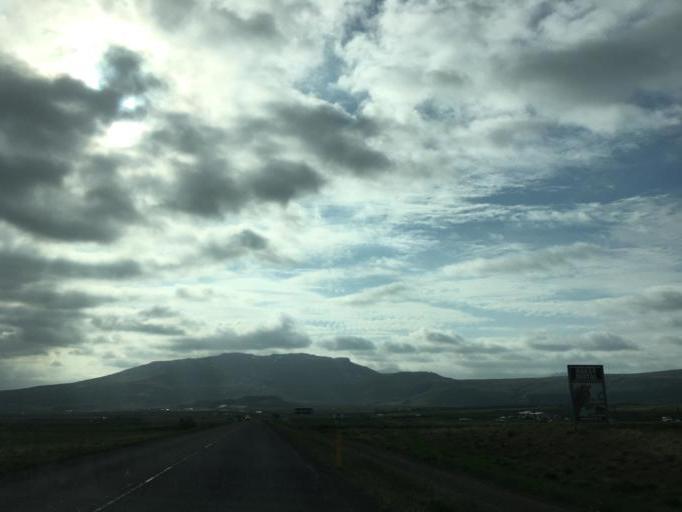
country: IS
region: South
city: Selfoss
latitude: 64.3093
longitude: -20.2273
